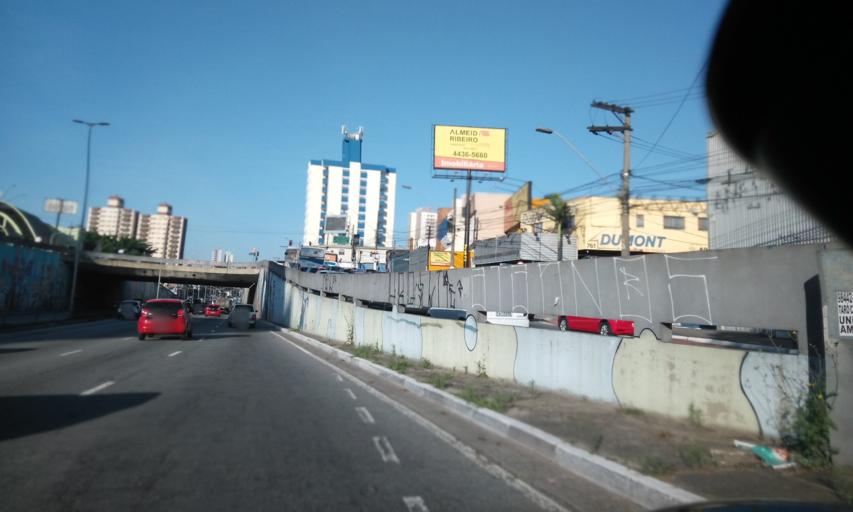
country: BR
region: Sao Paulo
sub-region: Santo Andre
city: Santo Andre
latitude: -23.6642
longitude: -46.5142
